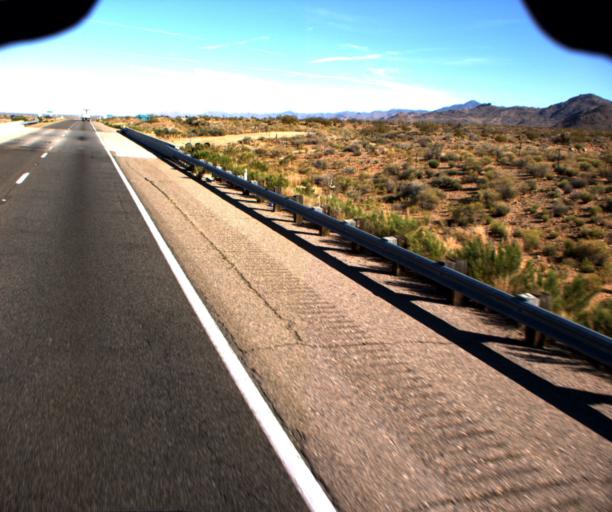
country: US
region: Arizona
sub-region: Mohave County
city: Golden Valley
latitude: 35.2481
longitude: -114.1513
